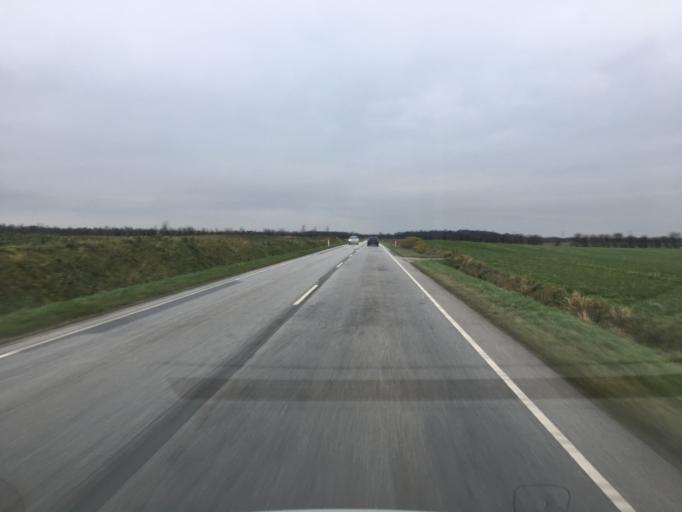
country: DK
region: South Denmark
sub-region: Aabenraa Kommune
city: Tinglev
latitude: 55.0047
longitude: 9.2476
